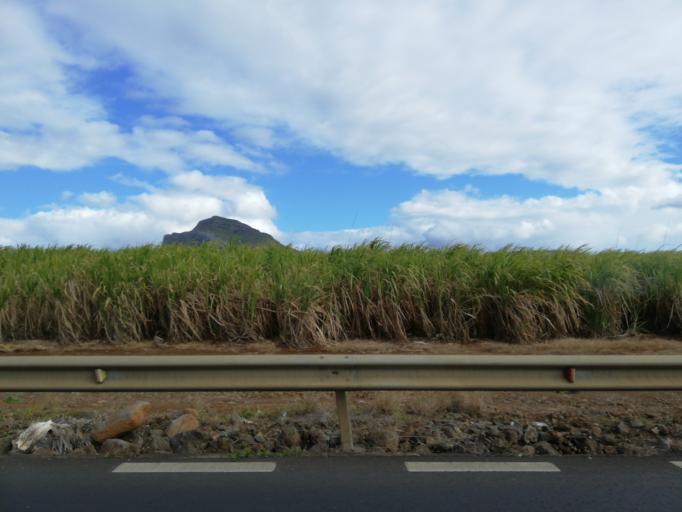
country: MU
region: Black River
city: Gros Cailloux
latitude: -20.2306
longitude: 57.4468
